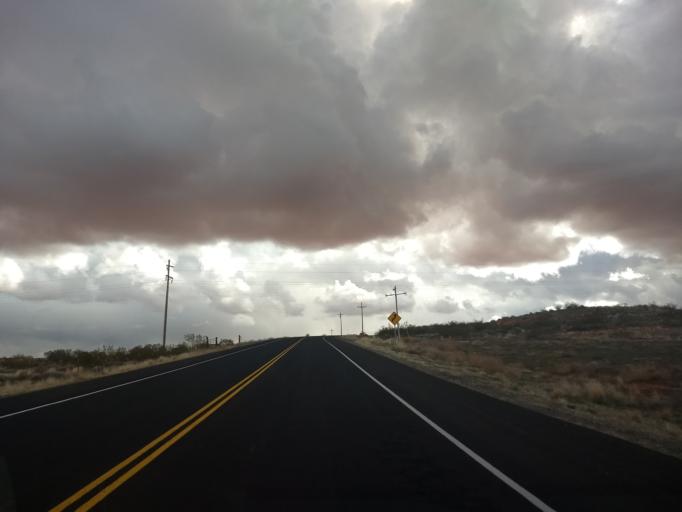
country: US
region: Utah
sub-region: Washington County
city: Hurricane
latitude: 37.1419
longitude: -113.3897
